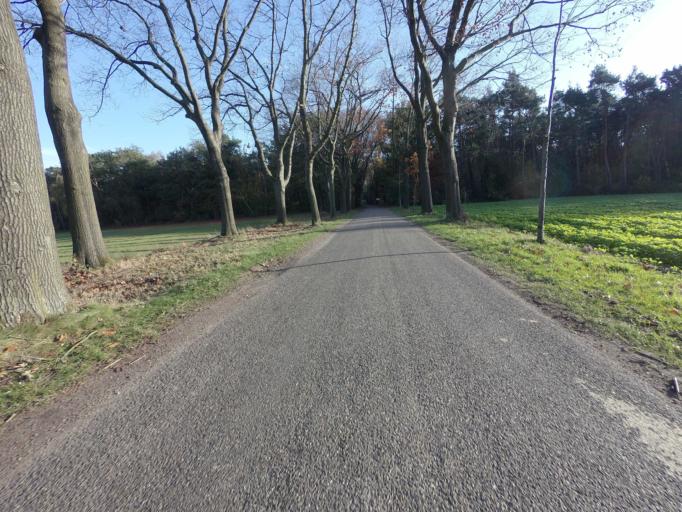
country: DE
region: North Rhine-Westphalia
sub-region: Regierungsbezirk Koln
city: Waldfeucht
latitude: 51.0932
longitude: 6.0063
